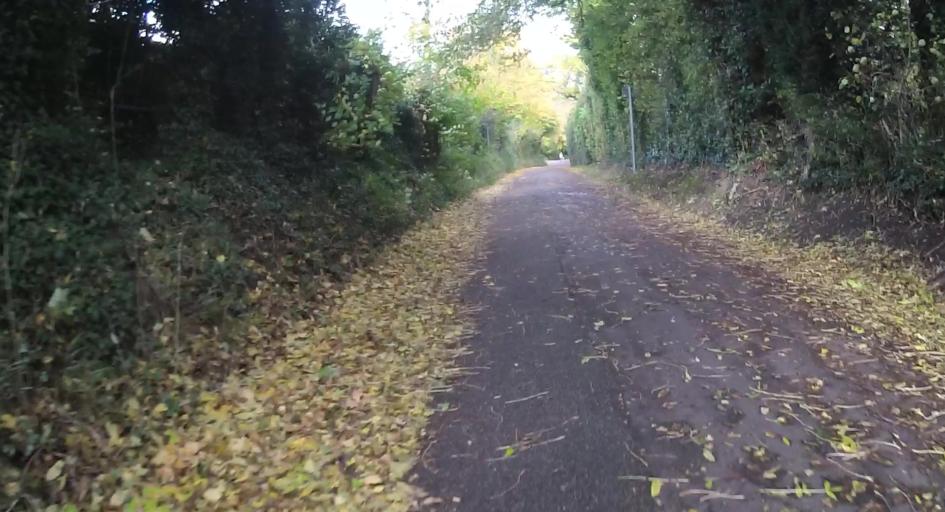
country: GB
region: England
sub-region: Hampshire
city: Old Basing
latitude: 51.2852
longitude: -1.0507
